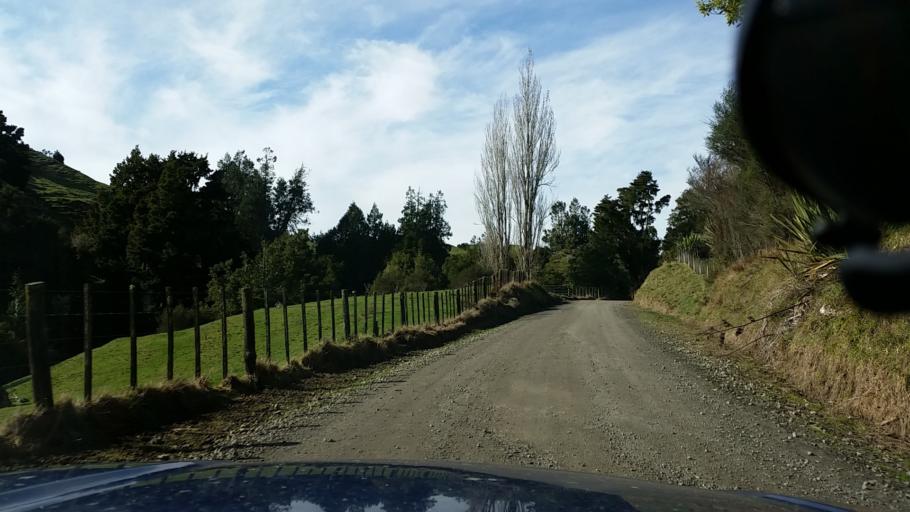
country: NZ
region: Taranaki
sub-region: New Plymouth District
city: Waitara
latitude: -39.0586
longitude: 174.7798
